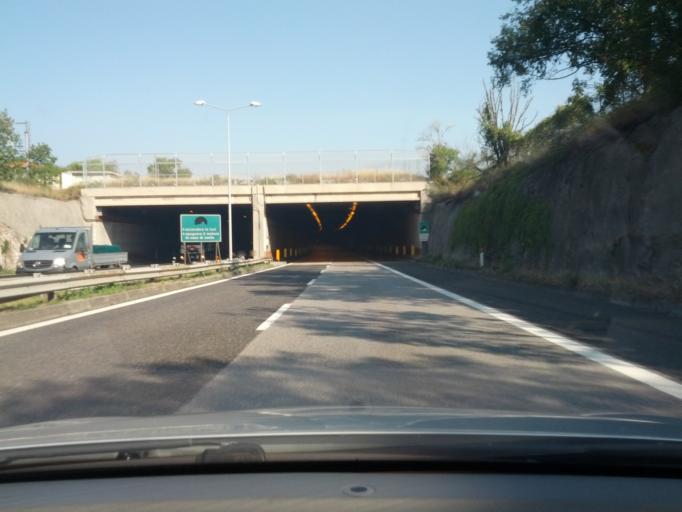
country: IT
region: Friuli Venezia Giulia
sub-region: Provincia di Trieste
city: Prosecco-Contovello
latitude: 45.7060
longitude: 13.7469
